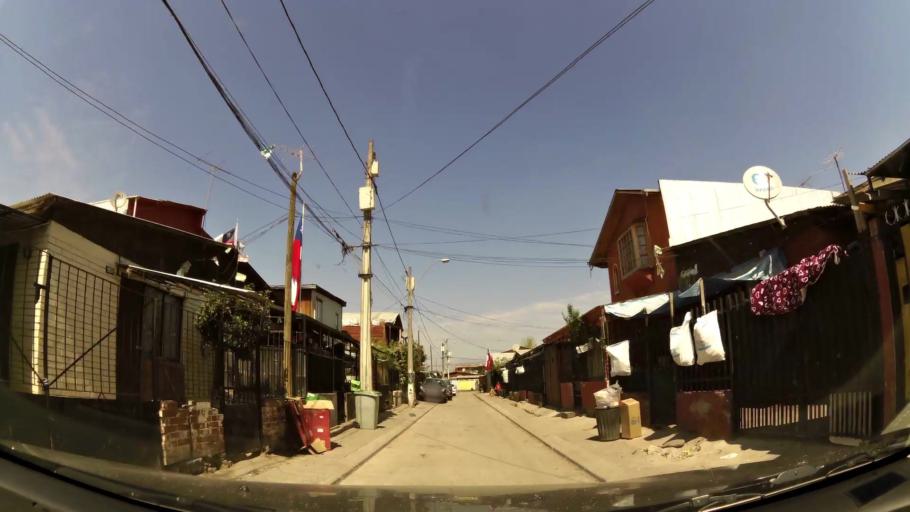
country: CL
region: Santiago Metropolitan
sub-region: Provincia de Santiago
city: La Pintana
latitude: -33.5897
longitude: -70.6274
